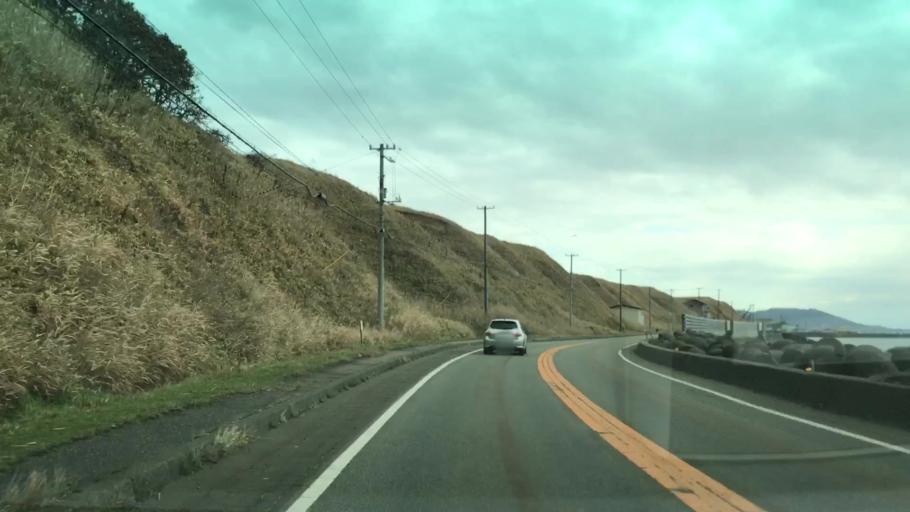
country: JP
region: Hokkaido
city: Shizunai-furukawacho
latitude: 42.0505
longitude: 143.0948
